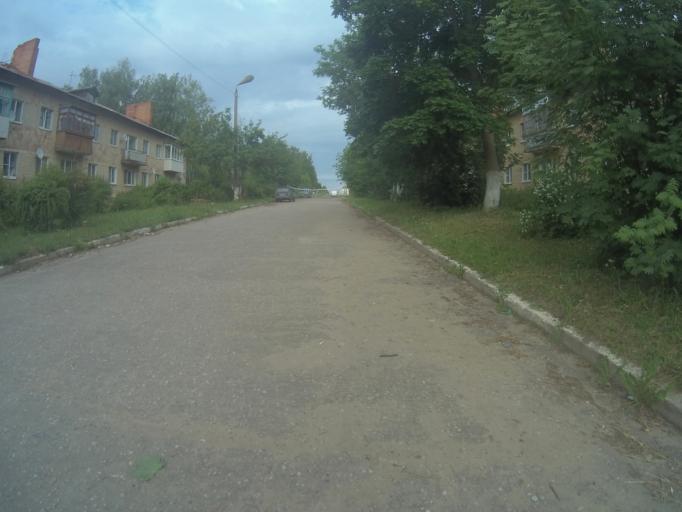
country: RU
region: Vladimir
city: Vladimir
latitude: 56.2227
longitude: 40.4146
